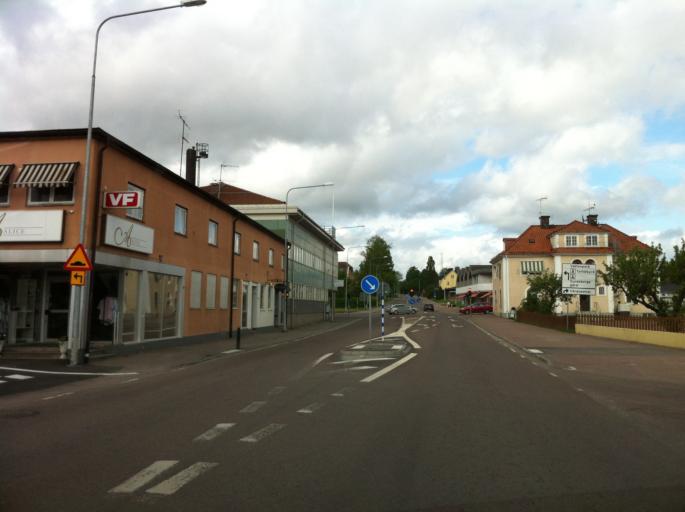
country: SE
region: Vaermland
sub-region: Sunne Kommun
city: Sunne
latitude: 59.8376
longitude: 13.1434
